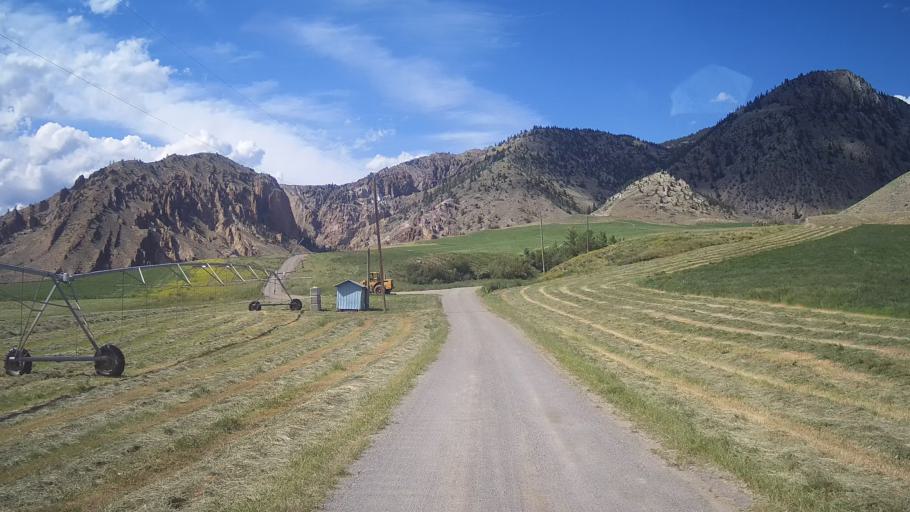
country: CA
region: British Columbia
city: Lillooet
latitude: 51.1877
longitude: -122.1188
